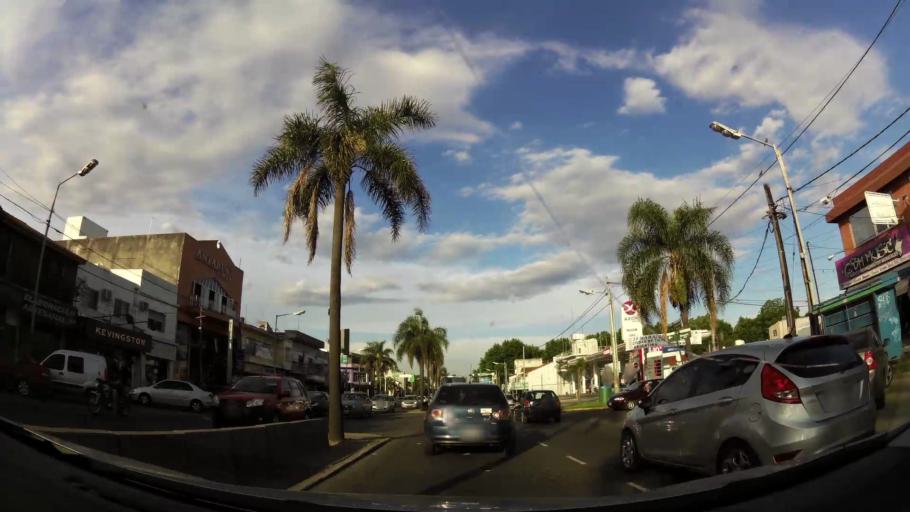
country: AR
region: Buenos Aires
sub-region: Partido de Tigre
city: Tigre
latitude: -34.4573
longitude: -58.6287
